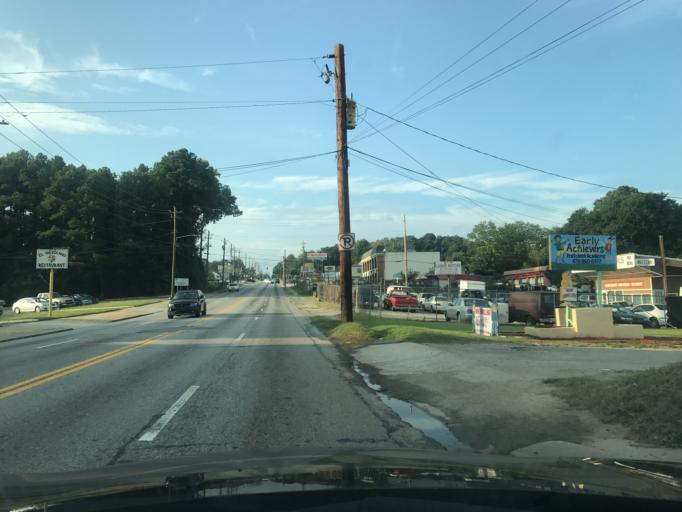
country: US
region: Georgia
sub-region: DeKalb County
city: Gresham Park
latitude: 33.7176
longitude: -84.3495
